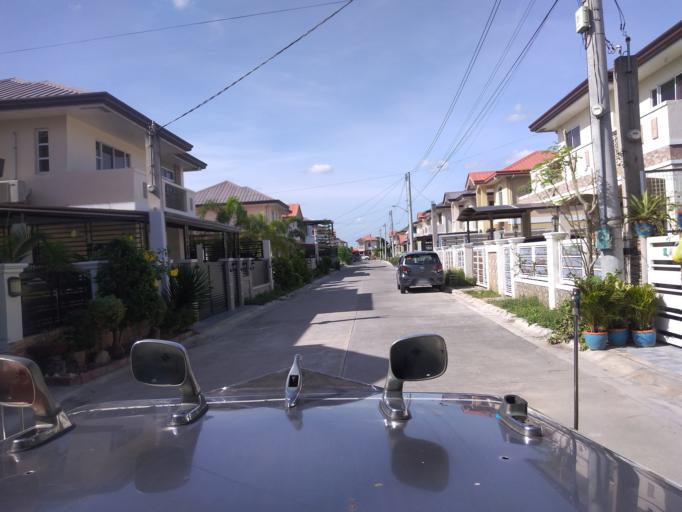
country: PH
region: Central Luzon
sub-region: Province of Pampanga
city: Magliman
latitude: 15.0237
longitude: 120.6604
